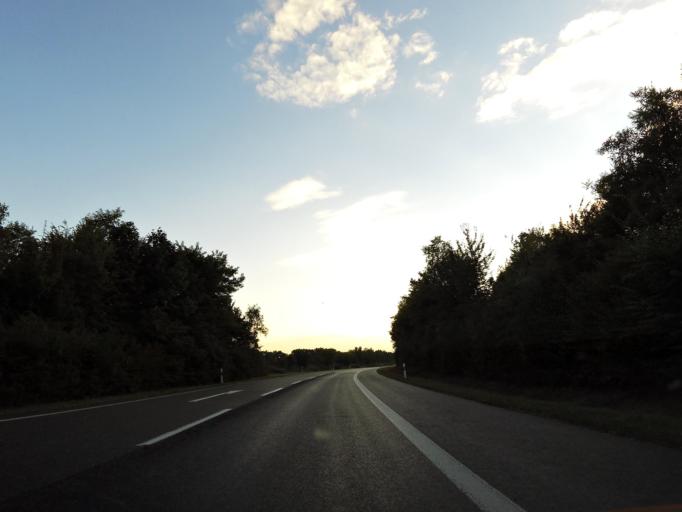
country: DE
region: Rheinland-Pfalz
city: Albig
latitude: 49.7744
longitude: 8.1073
